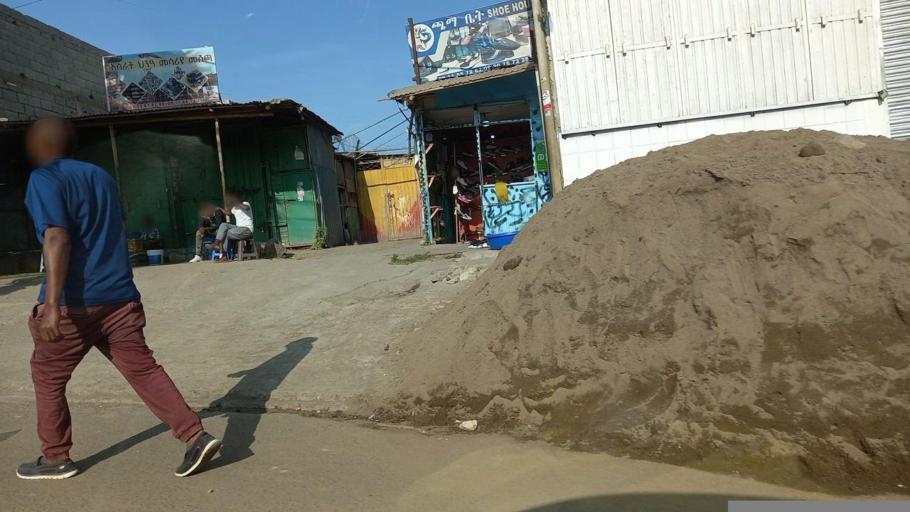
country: ET
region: Adis Abeba
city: Addis Ababa
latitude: 8.9368
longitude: 38.7459
